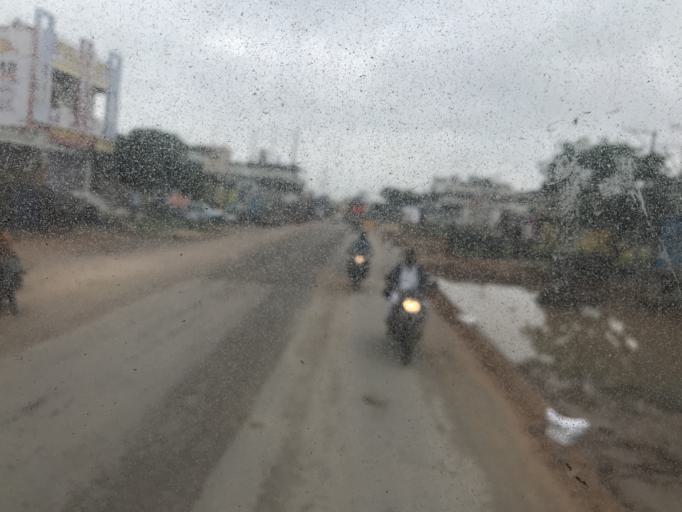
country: IN
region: Telangana
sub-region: Mahbubnagar
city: Mahbubnagar
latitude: 16.7739
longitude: 78.1278
